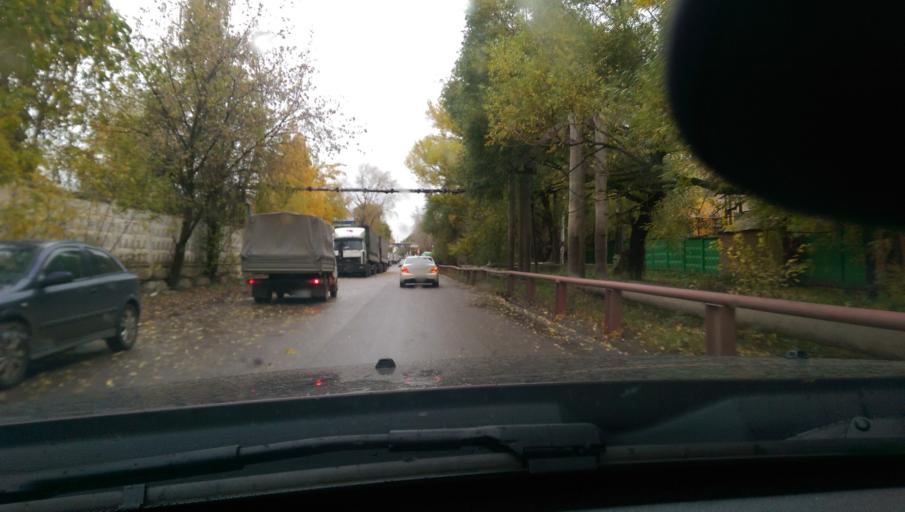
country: RU
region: Moscow
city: Altuf'yevskiy
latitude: 55.8881
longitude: 37.5735
